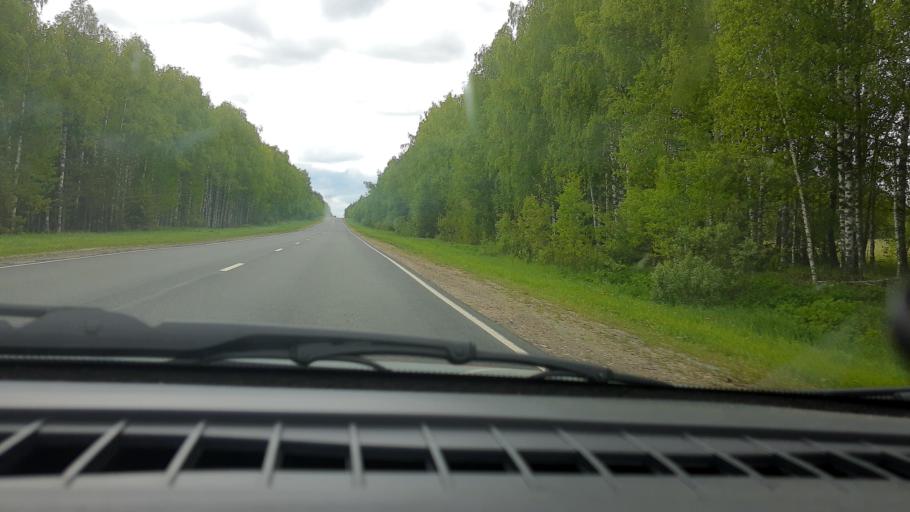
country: RU
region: Nizjnij Novgorod
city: Vladimirskoye
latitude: 56.9525
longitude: 45.0908
